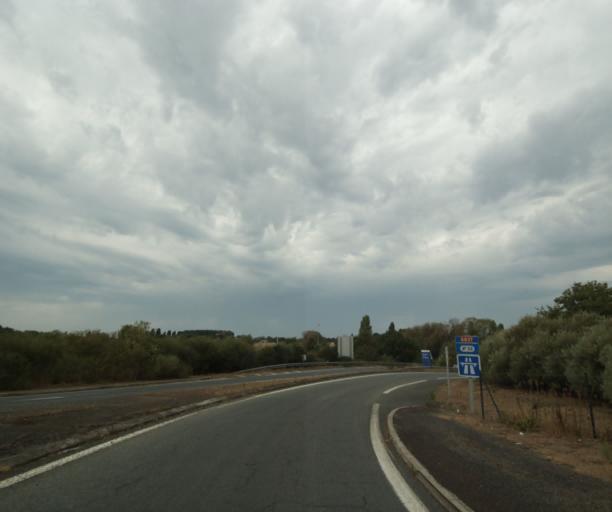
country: FR
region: Poitou-Charentes
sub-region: Departement de la Charente-Maritime
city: Breuil-Magne
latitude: 45.9612
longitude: -0.9587
